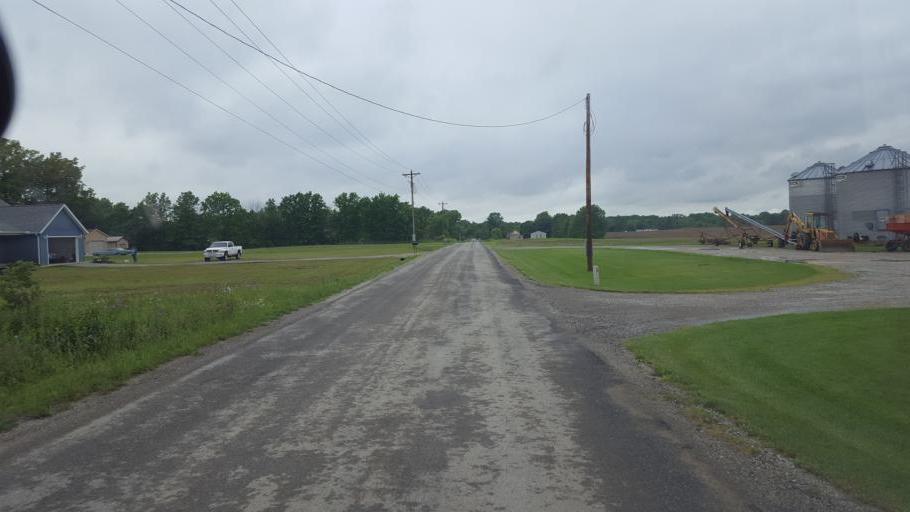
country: US
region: Ohio
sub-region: Morrow County
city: Mount Gilead
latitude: 40.4756
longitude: -82.7716
